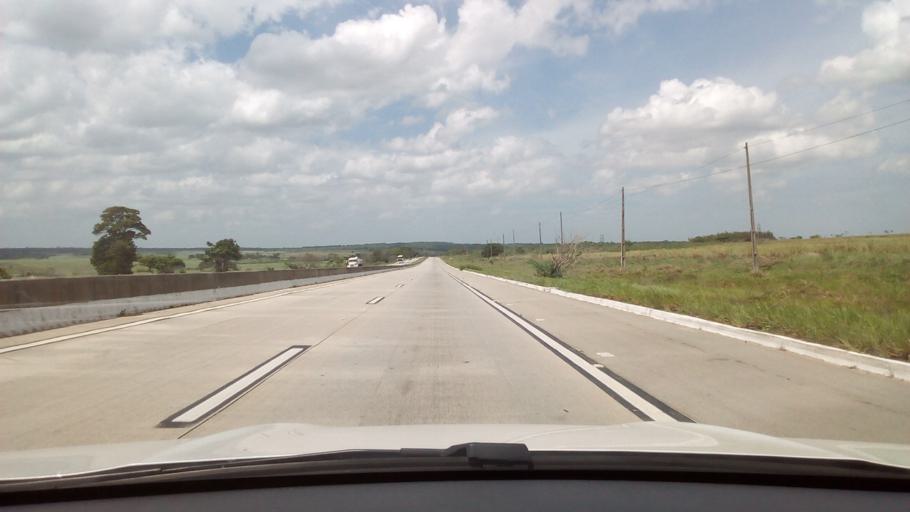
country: BR
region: Paraiba
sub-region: Mamanguape
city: Mamanguape
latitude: -6.7834
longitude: -35.1338
